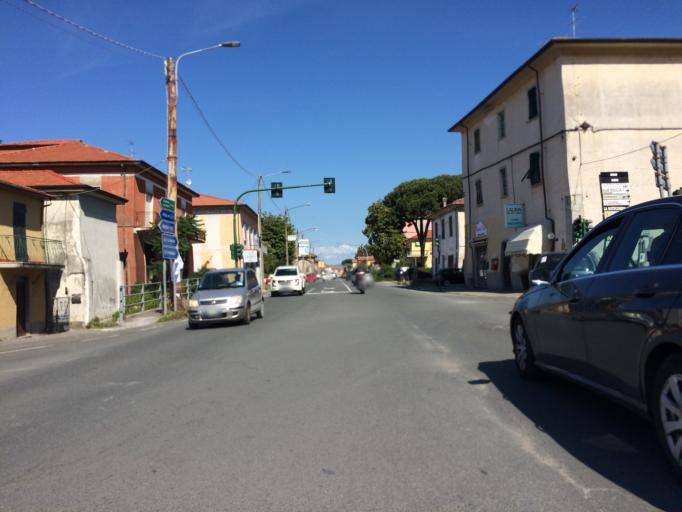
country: IT
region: Liguria
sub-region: Provincia di La Spezia
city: Casano-Dogana-Isola
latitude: 44.0661
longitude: 10.0317
